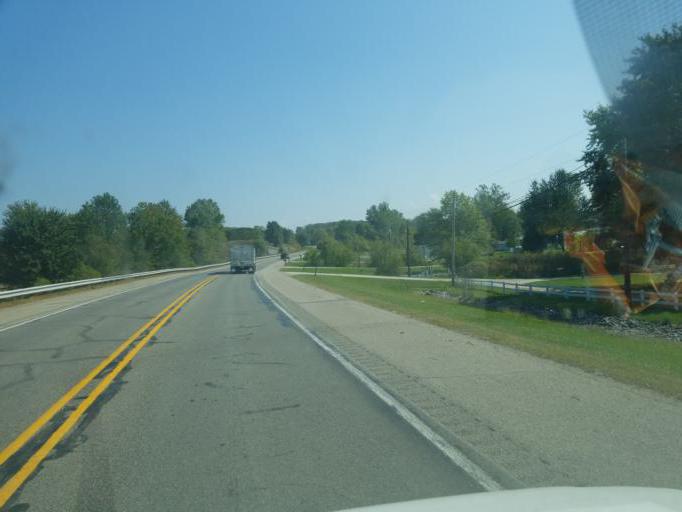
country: US
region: Indiana
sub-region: Steuben County
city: Angola
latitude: 41.6359
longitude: -85.0683
